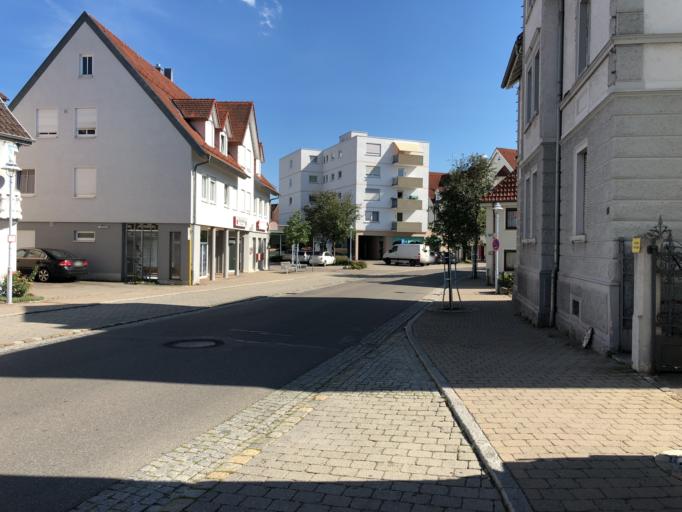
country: DE
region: Baden-Wuerttemberg
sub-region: Tuebingen Region
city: Bad Buchau
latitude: 48.0642
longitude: 9.6092
